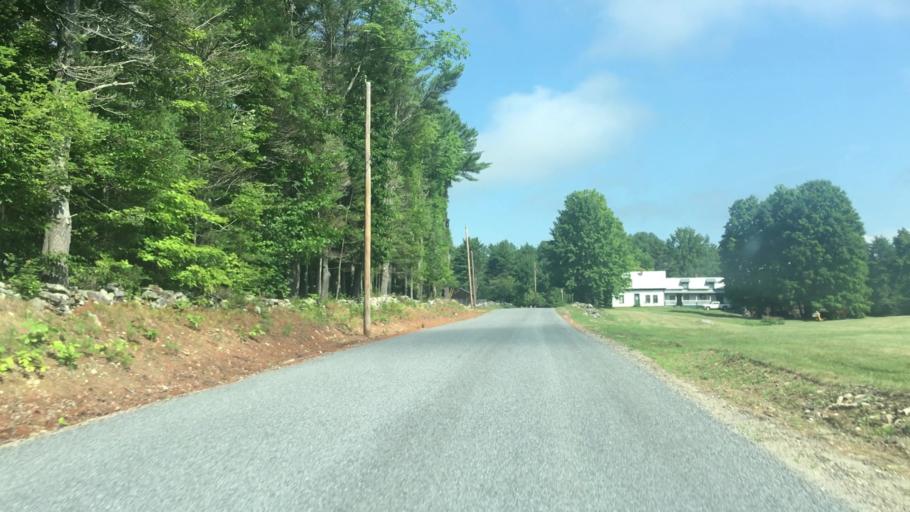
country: US
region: Maine
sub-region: Oxford County
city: Paris
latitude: 44.2891
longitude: -70.5234
